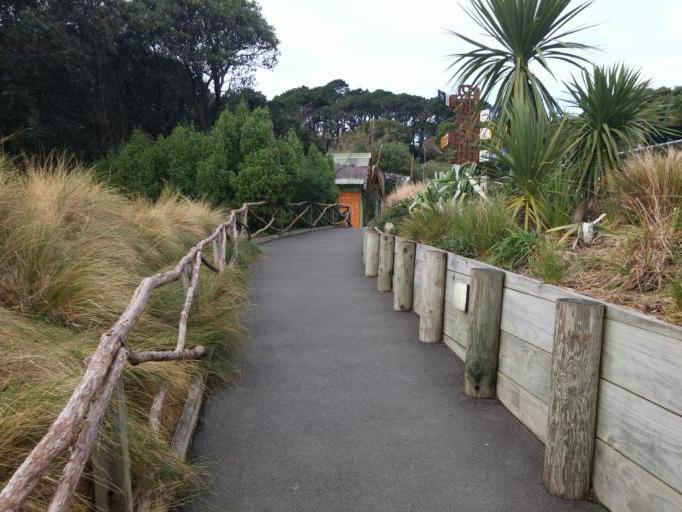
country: NZ
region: Wellington
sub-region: Wellington City
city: Brooklyn
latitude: -41.3204
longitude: 174.7844
